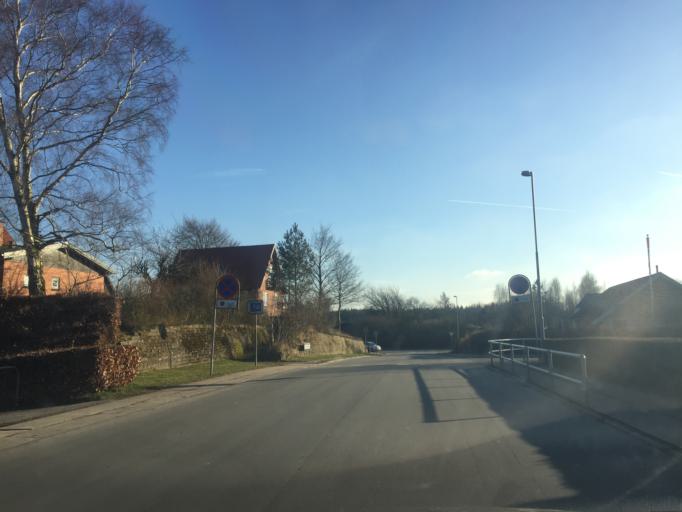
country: DK
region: South Denmark
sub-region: Nordfyns Kommune
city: Sonderso
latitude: 55.4445
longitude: 10.1928
